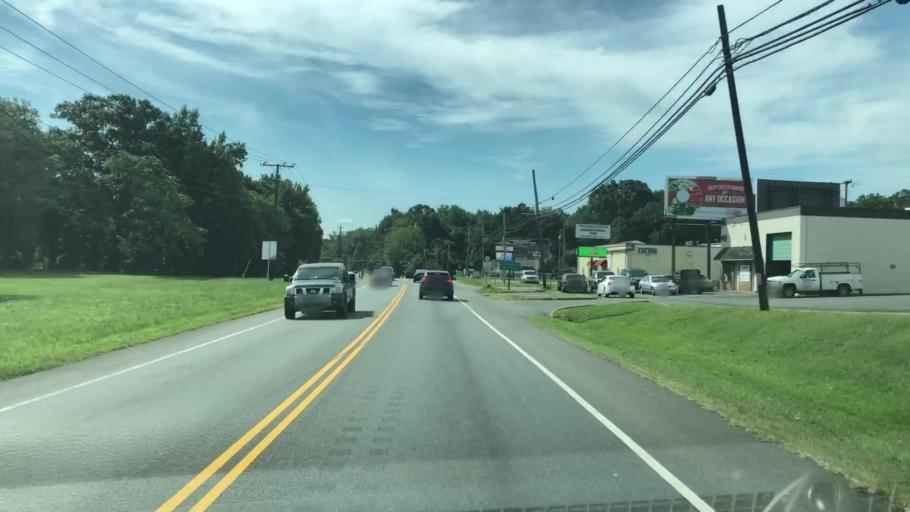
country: US
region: Virginia
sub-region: City of Fredericksburg
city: Fredericksburg
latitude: 38.2781
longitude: -77.4527
